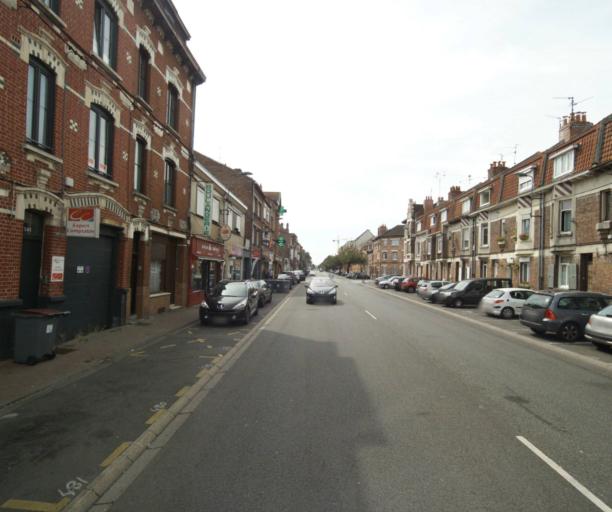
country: FR
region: Nord-Pas-de-Calais
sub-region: Departement du Nord
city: Wattignies
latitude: 50.6110
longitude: 3.0458
